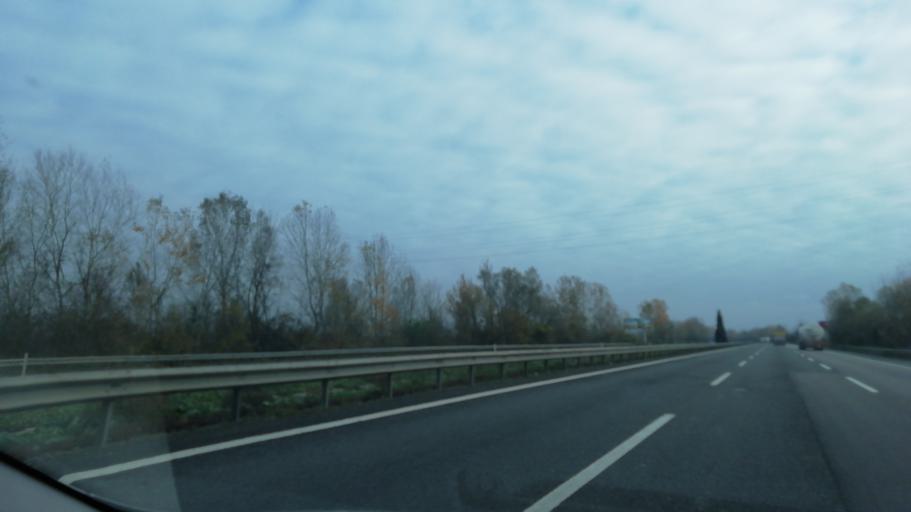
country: TR
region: Sakarya
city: Akyazi
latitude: 40.7232
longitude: 30.6171
